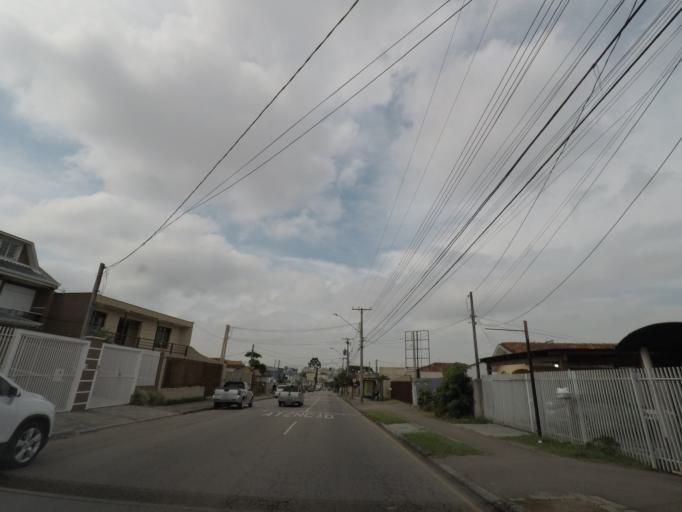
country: BR
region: Parana
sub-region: Curitiba
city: Curitiba
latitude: -25.4963
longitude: -49.2847
